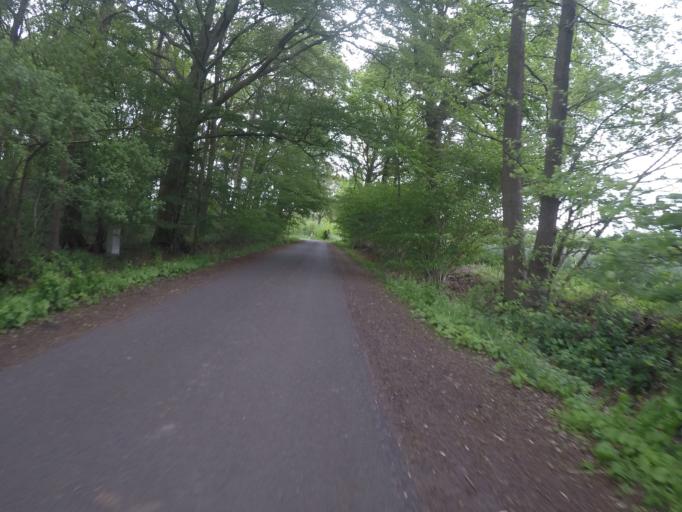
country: DE
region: Schleswig-Holstein
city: Bonningstedt
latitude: 53.6704
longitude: 9.9291
